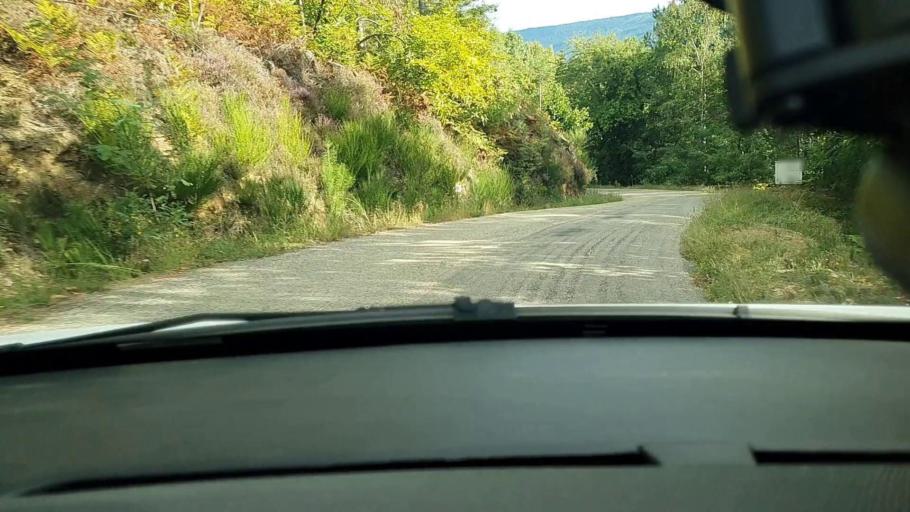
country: FR
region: Languedoc-Roussillon
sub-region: Departement du Gard
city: Besseges
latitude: 44.3505
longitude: 3.9817
